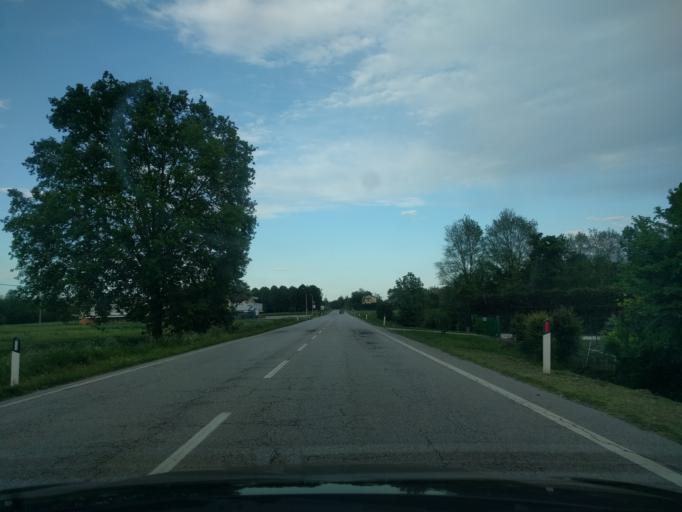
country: IT
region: Veneto
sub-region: Provincia di Rovigo
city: Canaro
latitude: 44.9308
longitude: 11.7165
